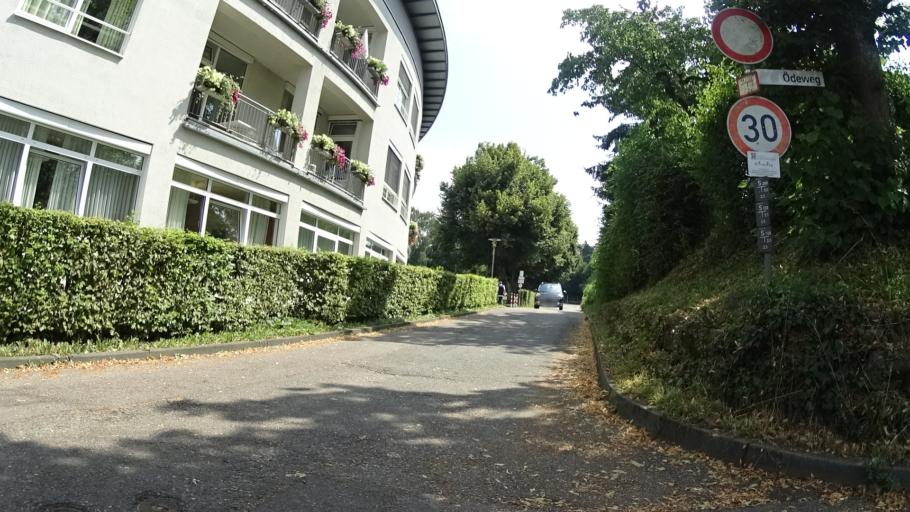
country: DE
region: Baden-Wuerttemberg
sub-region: Regierungsbezirk Stuttgart
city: Goeppingen
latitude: 48.7014
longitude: 9.6418
